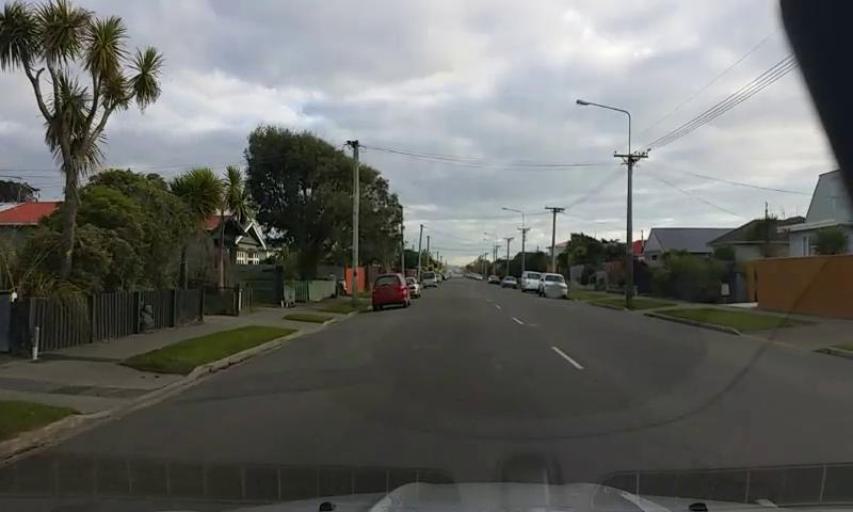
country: NZ
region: Canterbury
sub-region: Christchurch City
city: Christchurch
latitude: -43.5292
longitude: 172.7352
